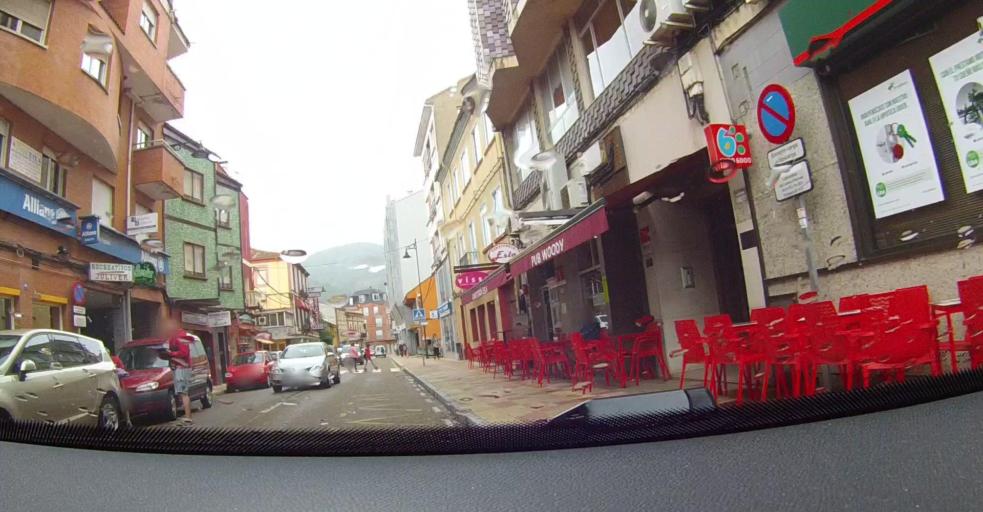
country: ES
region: Castille and Leon
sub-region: Provincia de Leon
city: Cistierna
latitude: 42.8031
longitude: -5.1278
